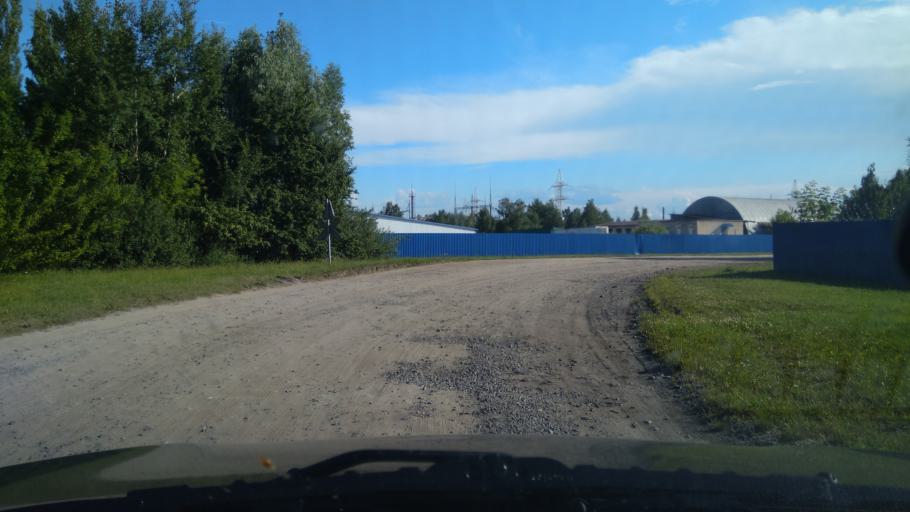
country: BY
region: Brest
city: Byelaazyorsk
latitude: 52.4577
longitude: 25.1884
